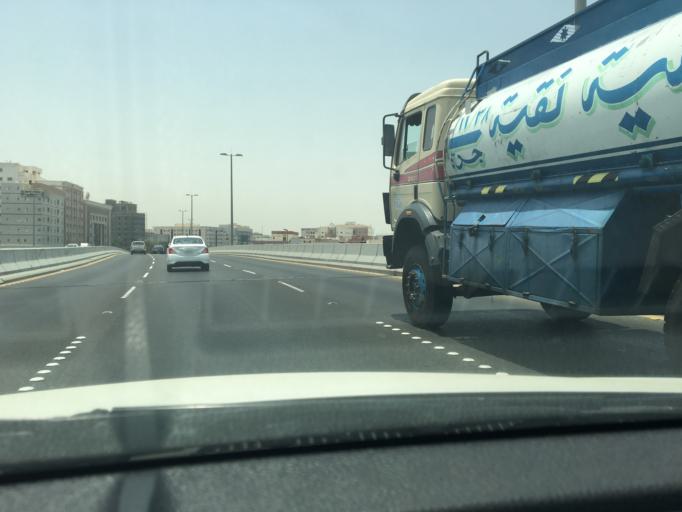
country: SA
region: Makkah
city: Jeddah
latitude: 21.5676
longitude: 39.1831
